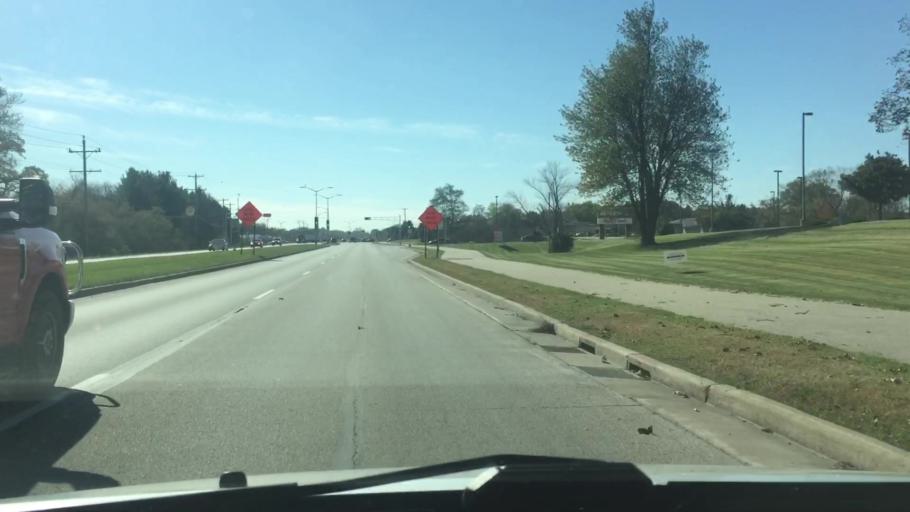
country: US
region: Wisconsin
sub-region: Waukesha County
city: Waukesha
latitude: 42.9917
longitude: -88.2645
